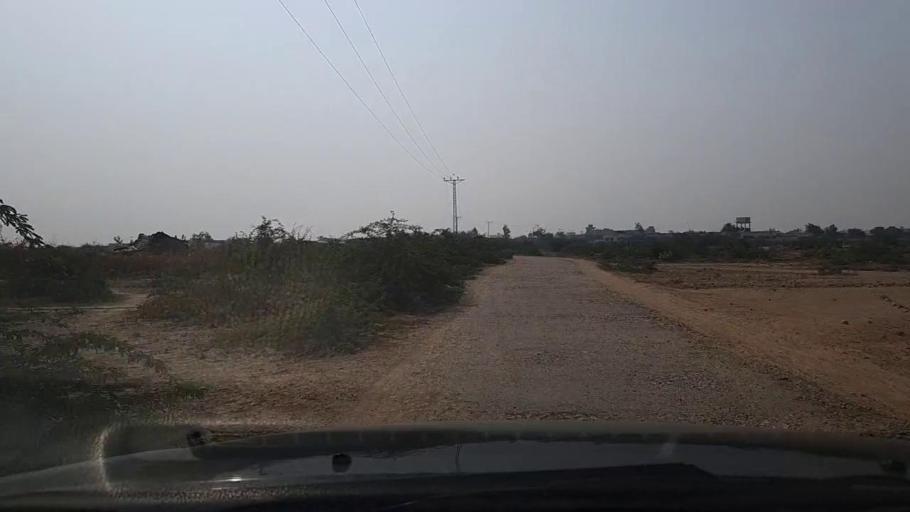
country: PK
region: Sindh
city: Thatta
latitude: 24.7443
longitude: 67.9004
